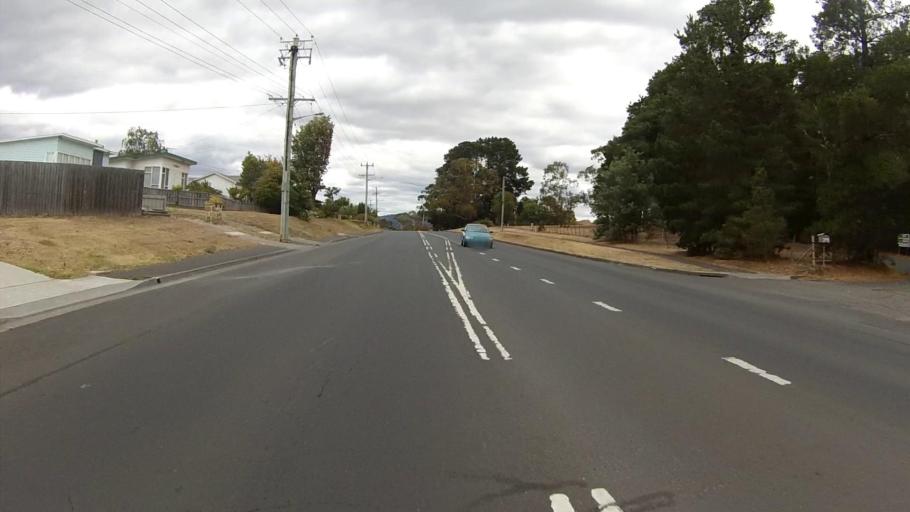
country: AU
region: Tasmania
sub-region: Glenorchy
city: Austins Ferry
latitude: -42.7715
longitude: 147.2475
